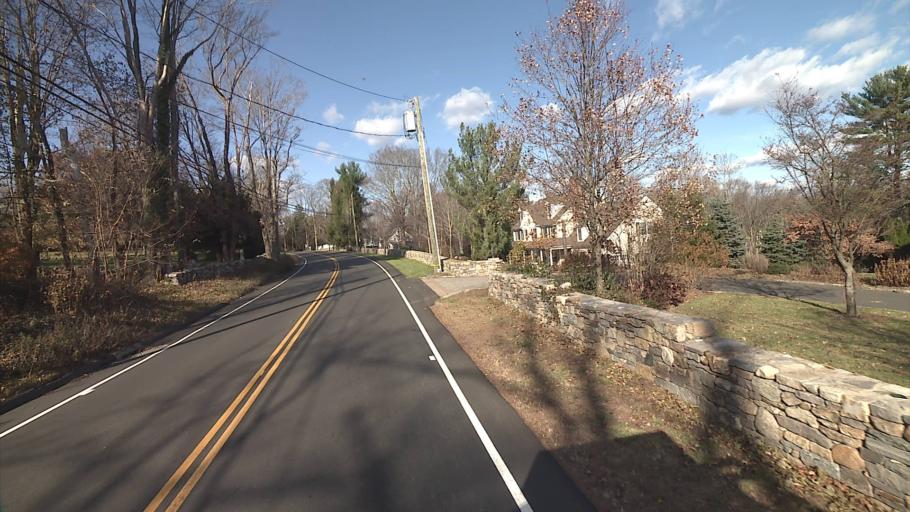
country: US
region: Connecticut
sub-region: Fairfield County
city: Wilton
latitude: 41.1824
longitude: -73.3939
